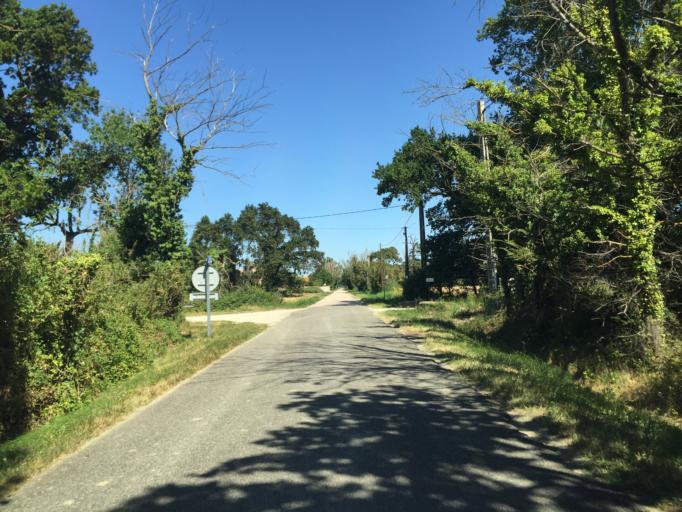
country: FR
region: Provence-Alpes-Cote d'Azur
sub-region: Departement du Vaucluse
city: Bedarrides
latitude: 44.0604
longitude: 4.8942
